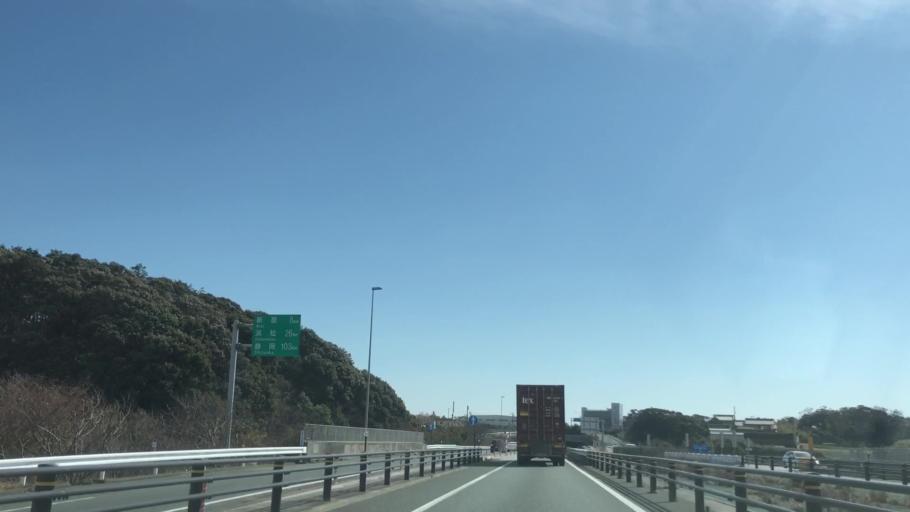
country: JP
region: Shizuoka
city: Kosai-shi
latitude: 34.6891
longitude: 137.4897
